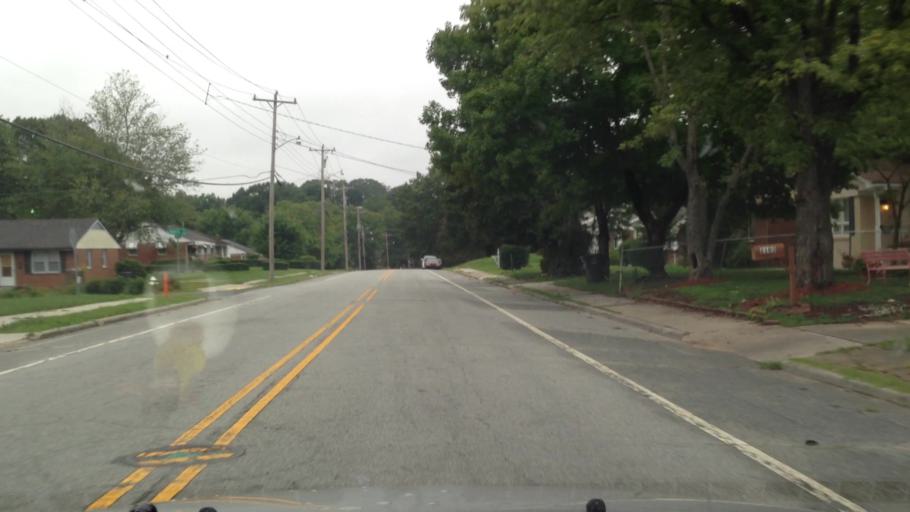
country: US
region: North Carolina
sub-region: Guilford County
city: Greensboro
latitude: 36.0538
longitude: -79.7588
